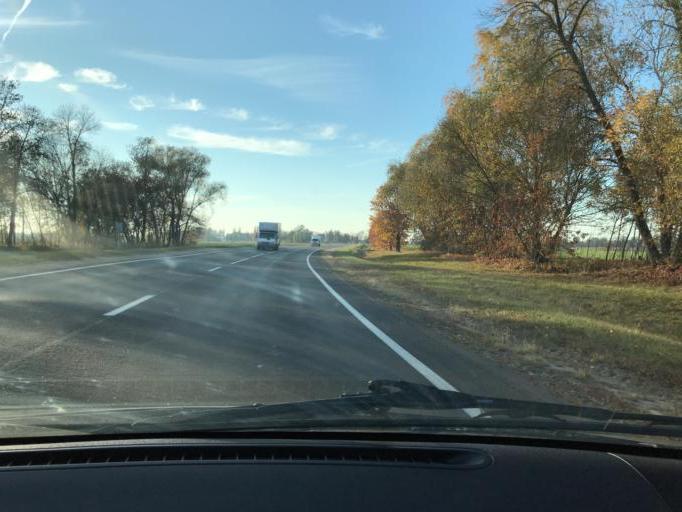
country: BY
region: Brest
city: Horad Kobryn
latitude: 52.2171
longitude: 24.5127
